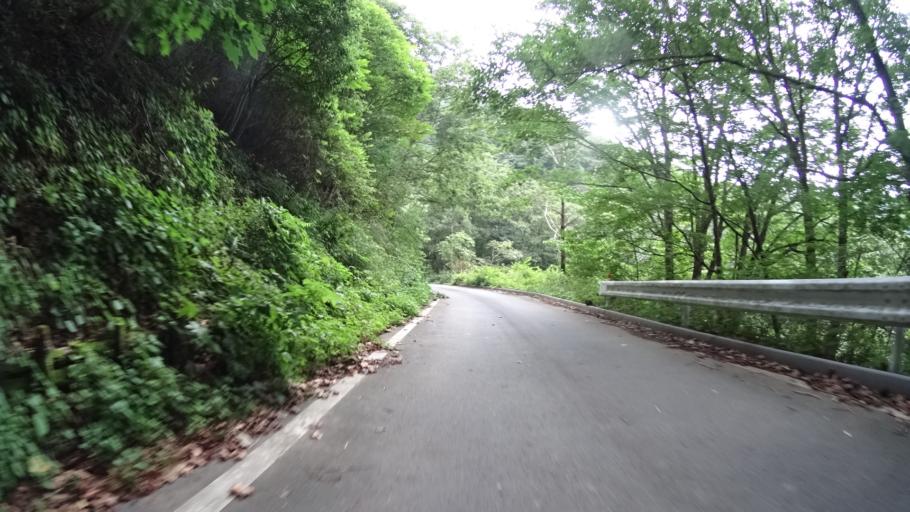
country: JP
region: Yamanashi
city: Nirasaki
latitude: 35.8076
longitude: 138.5471
